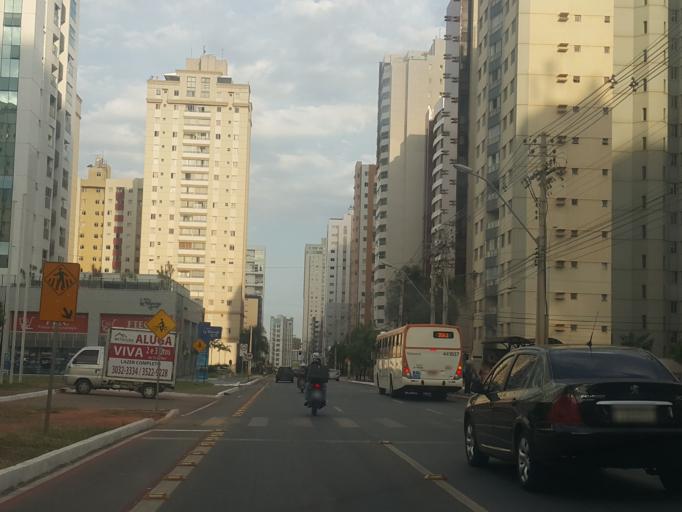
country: BR
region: Federal District
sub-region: Brasilia
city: Brasilia
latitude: -15.8375
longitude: -48.0385
